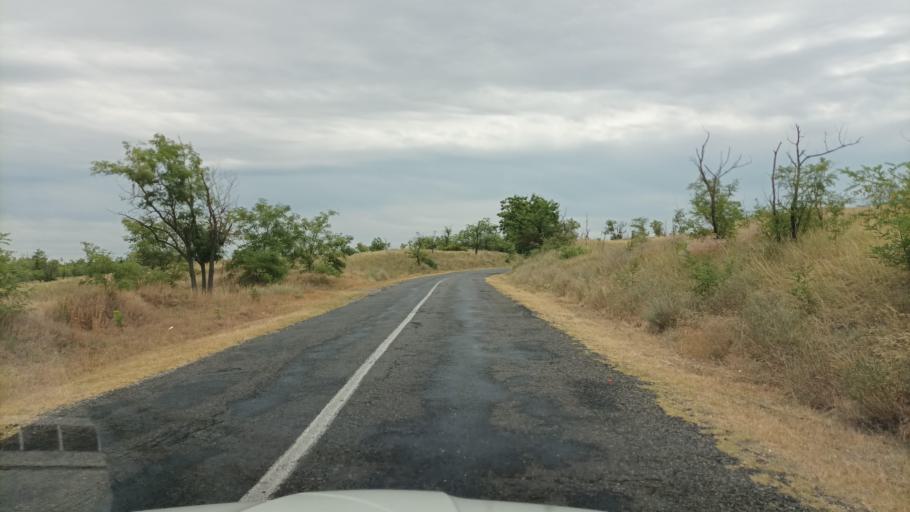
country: HU
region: Pest
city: Orkeny
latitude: 47.1185
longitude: 19.3567
